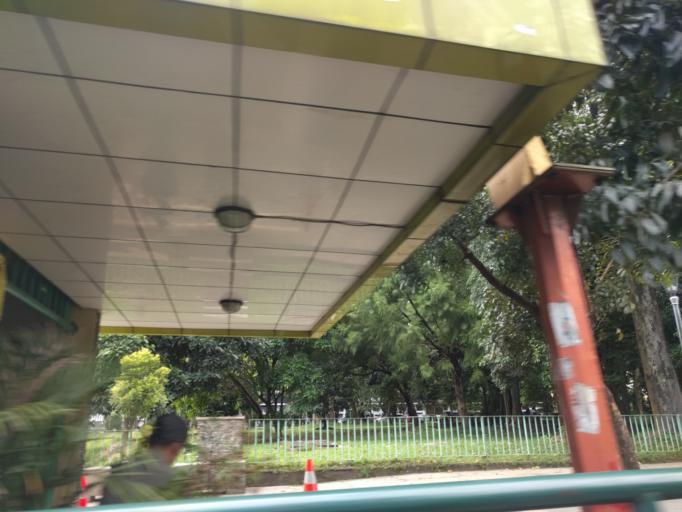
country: ID
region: West Java
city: Bogor
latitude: -6.6007
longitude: 106.8051
